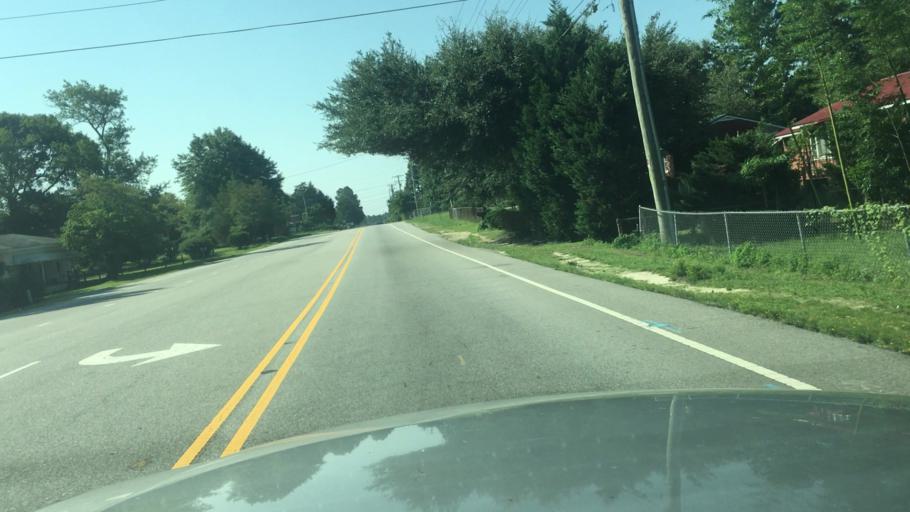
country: US
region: North Carolina
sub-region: Cumberland County
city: Spring Lake
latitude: 35.1498
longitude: -78.9118
